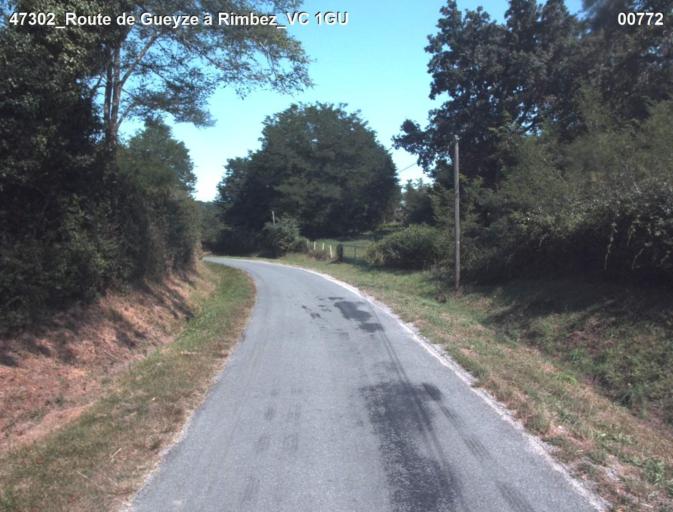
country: FR
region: Midi-Pyrenees
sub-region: Departement du Gers
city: Montreal
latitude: 44.0429
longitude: 0.1270
